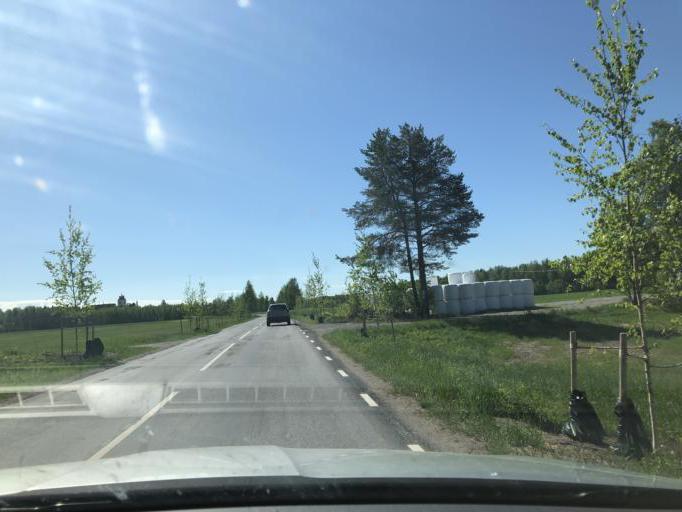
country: SE
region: Norrbotten
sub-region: Lulea Kommun
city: Gammelstad
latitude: 65.6537
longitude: 22.0164
